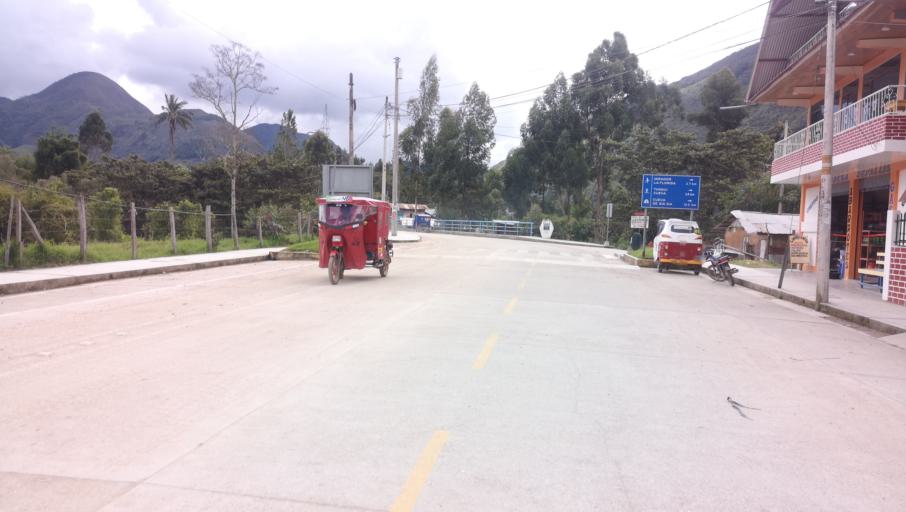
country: PE
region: Pasco
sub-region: Provincia de Oxapampa
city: Oxapampa
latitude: -10.5868
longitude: -75.4062
